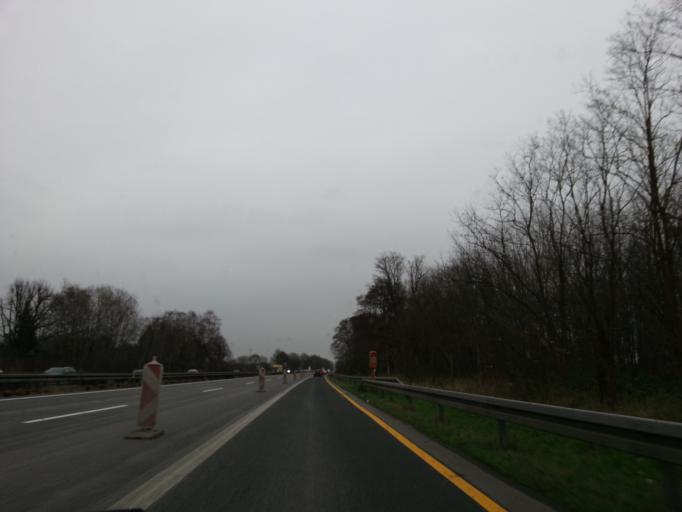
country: DE
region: North Rhine-Westphalia
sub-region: Regierungsbezirk Munster
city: Isselburg
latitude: 51.8205
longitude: 6.4274
